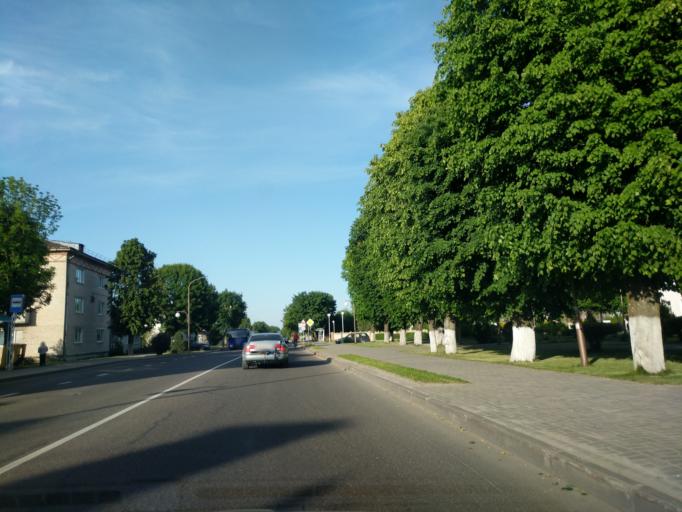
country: BY
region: Grodnenskaya
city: Ashmyany
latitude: 54.4289
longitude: 25.9465
